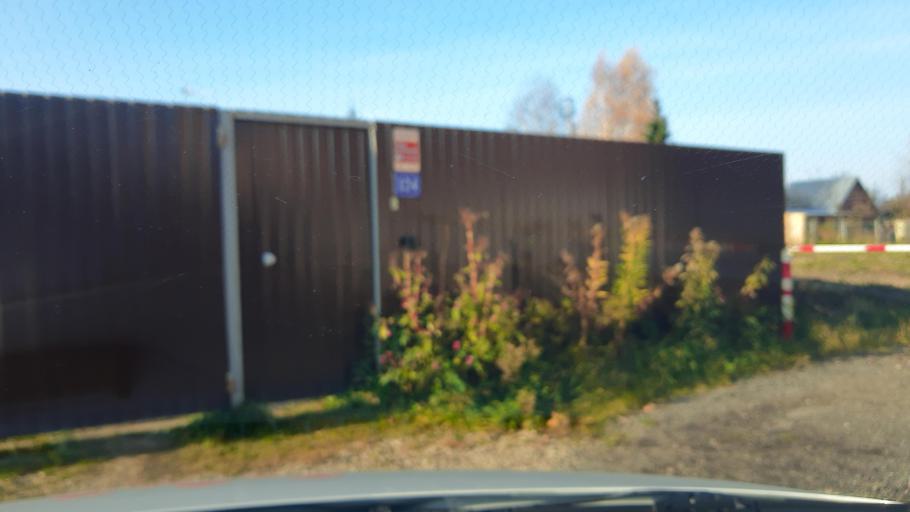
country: RU
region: Moskovskaya
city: Dubrovitsy
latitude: 55.4883
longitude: 37.4904
